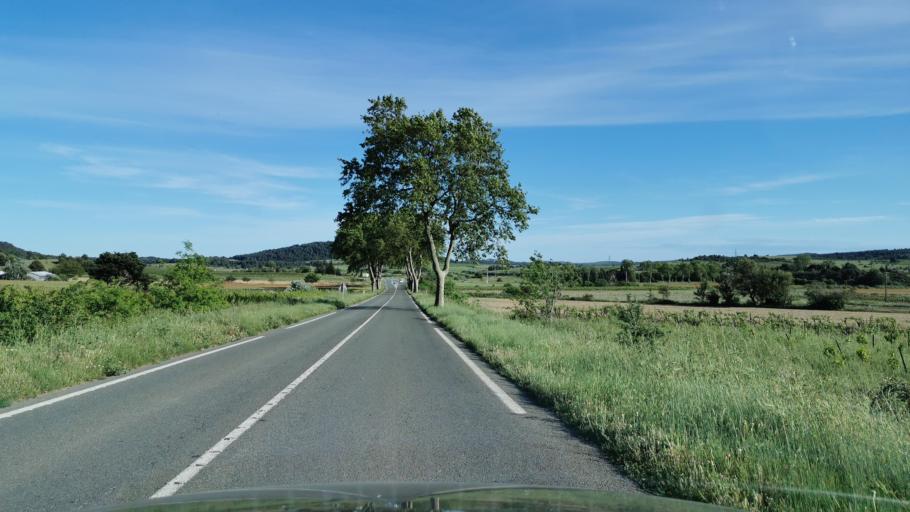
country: FR
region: Languedoc-Roussillon
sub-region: Departement de l'Aude
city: Marcorignan
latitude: 43.2204
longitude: 2.9262
